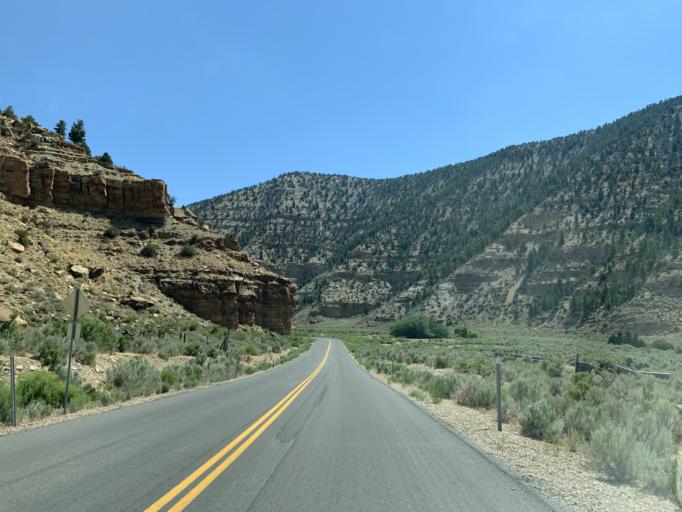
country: US
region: Utah
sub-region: Carbon County
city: East Carbon City
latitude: 39.7853
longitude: -110.3997
